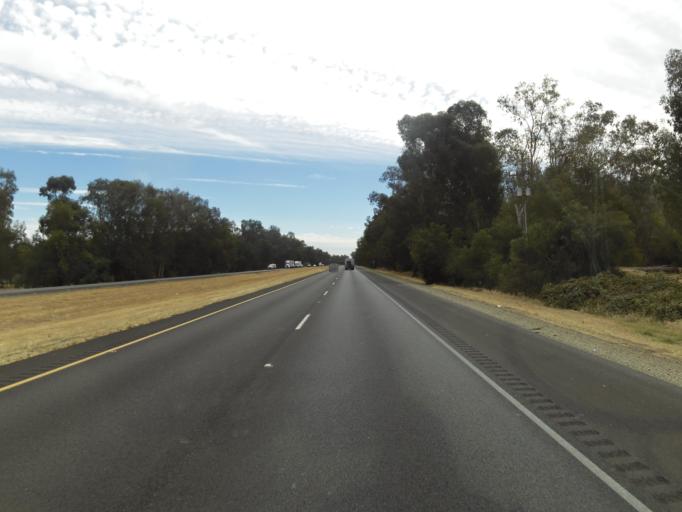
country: US
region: California
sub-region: Yolo County
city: Dunnigan
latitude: 38.9021
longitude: -121.9850
